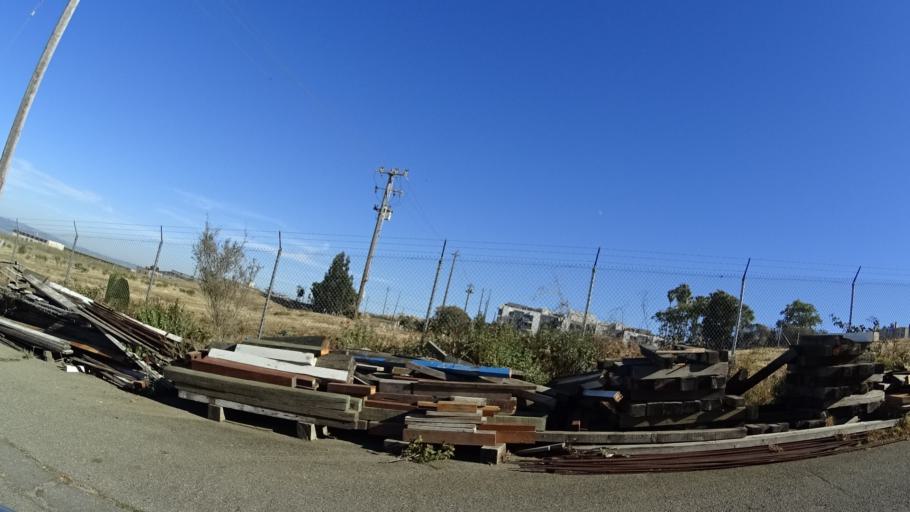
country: US
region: California
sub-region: San Mateo County
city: Brisbane
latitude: 37.7304
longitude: -122.3716
